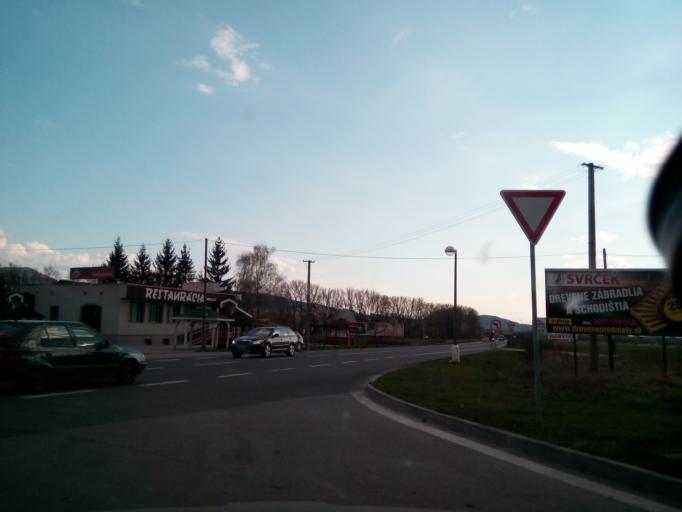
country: SK
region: Zilinsky
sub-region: Okres Zilina
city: Vrutky
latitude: 49.1175
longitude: 19.0276
